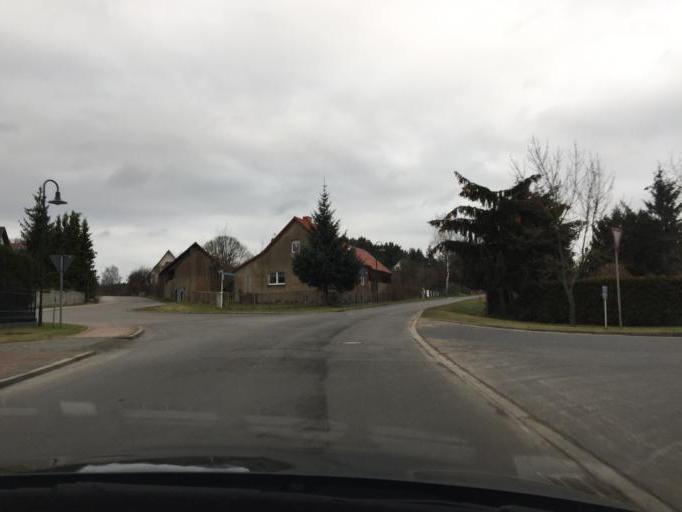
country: DE
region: Brandenburg
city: Gross Lindow
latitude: 52.1110
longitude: 14.5014
